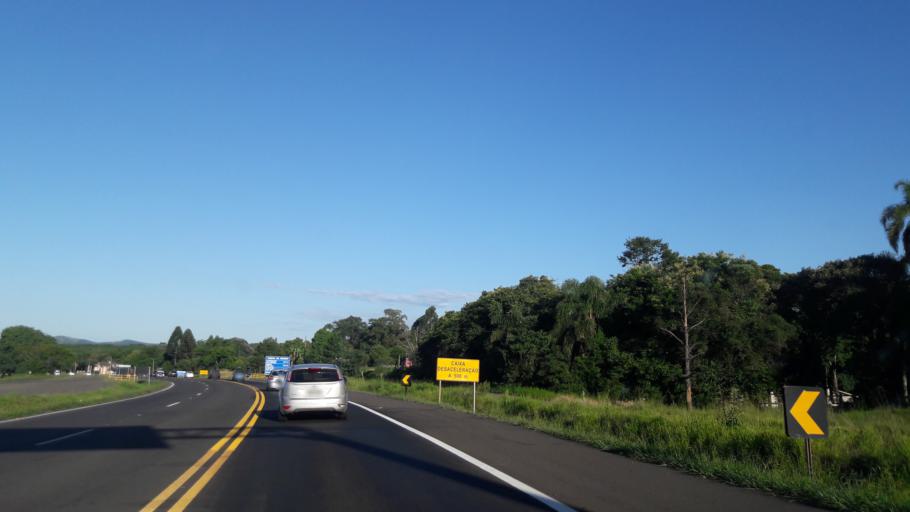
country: BR
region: Parana
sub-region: Prudentopolis
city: Prudentopolis
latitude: -25.3132
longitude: -51.1748
